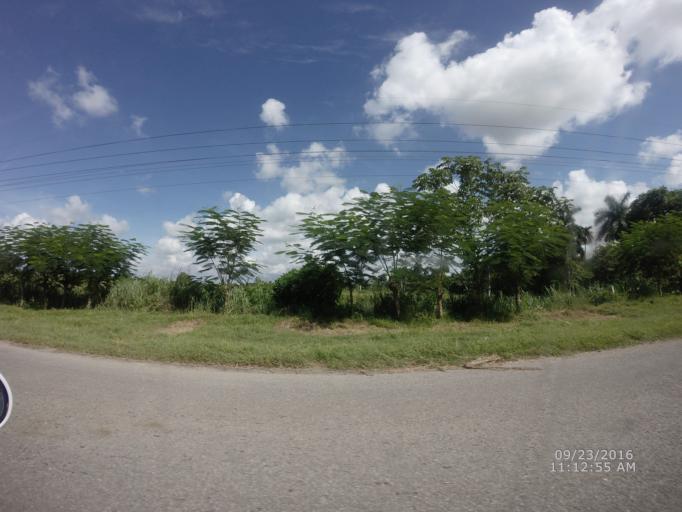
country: CU
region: La Habana
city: Arroyo Naranjo
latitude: 23.0305
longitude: -82.2905
